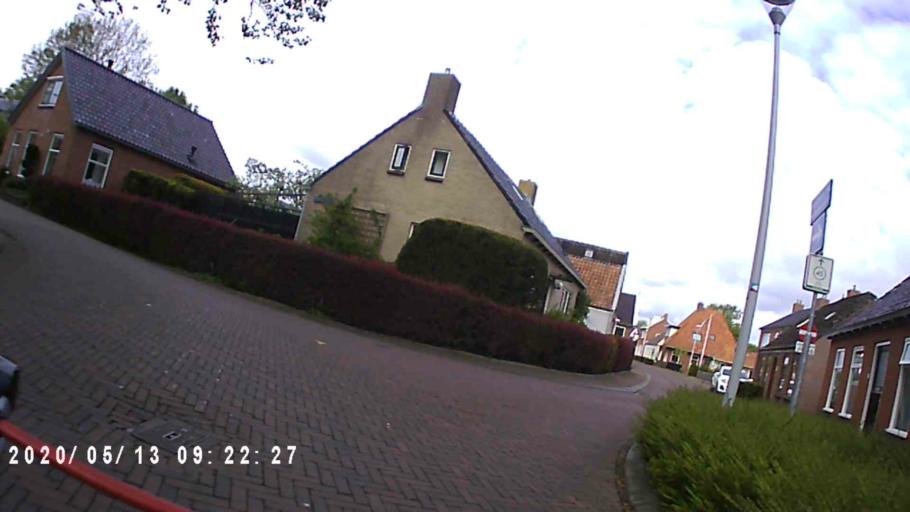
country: NL
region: Groningen
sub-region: Gemeente Zuidhorn
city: Noordhorn
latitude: 53.2625
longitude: 6.3962
